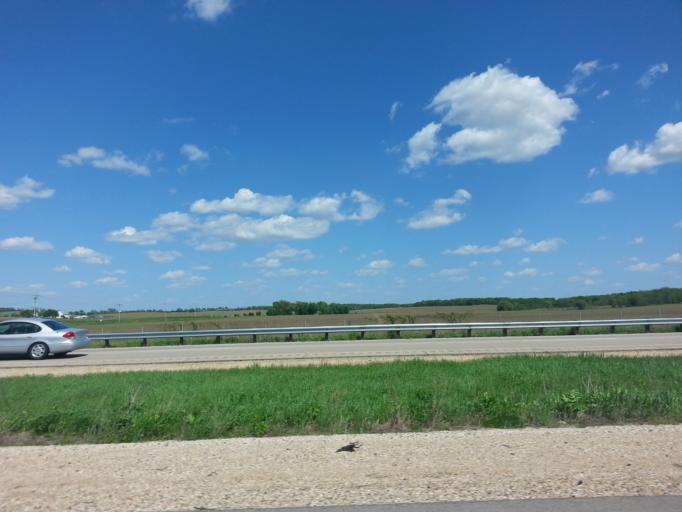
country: US
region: Wisconsin
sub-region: Rock County
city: Beloit
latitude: 42.5458
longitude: -88.9750
